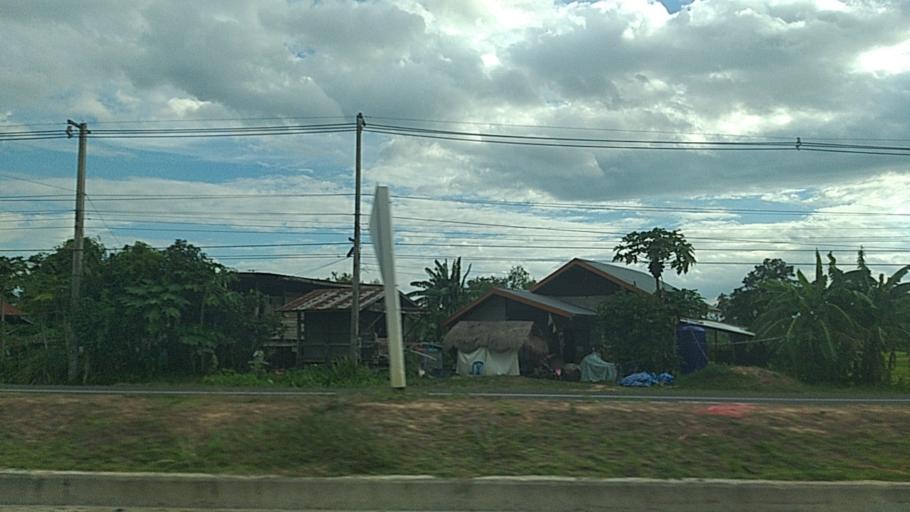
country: TH
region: Surin
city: Prasat
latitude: 14.5654
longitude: 103.4937
